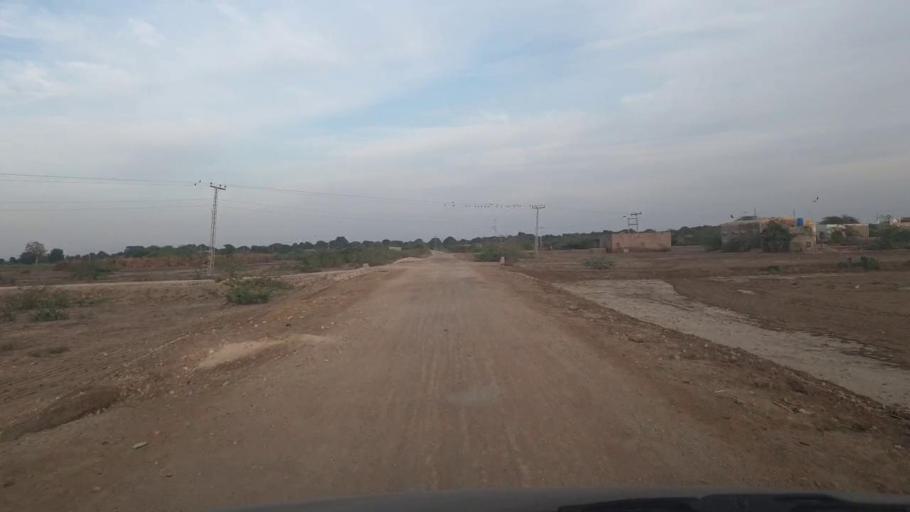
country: PK
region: Sindh
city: Kunri
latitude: 25.2385
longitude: 69.5547
